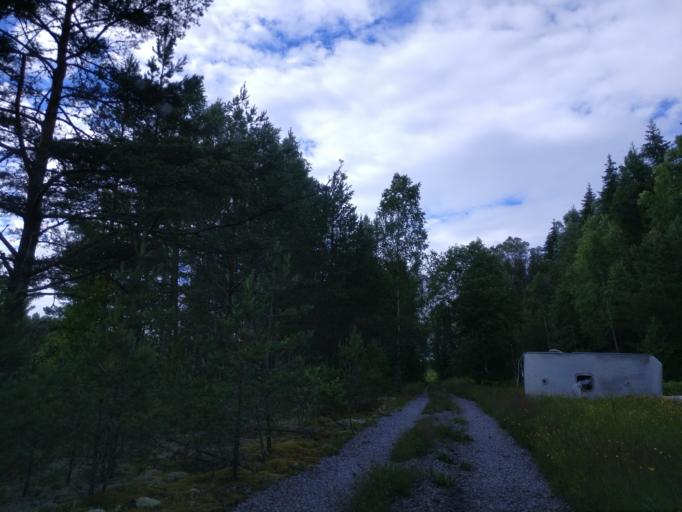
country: SE
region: Vaermland
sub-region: Hagfors Kommun
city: Ekshaerad
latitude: 60.0414
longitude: 13.5297
